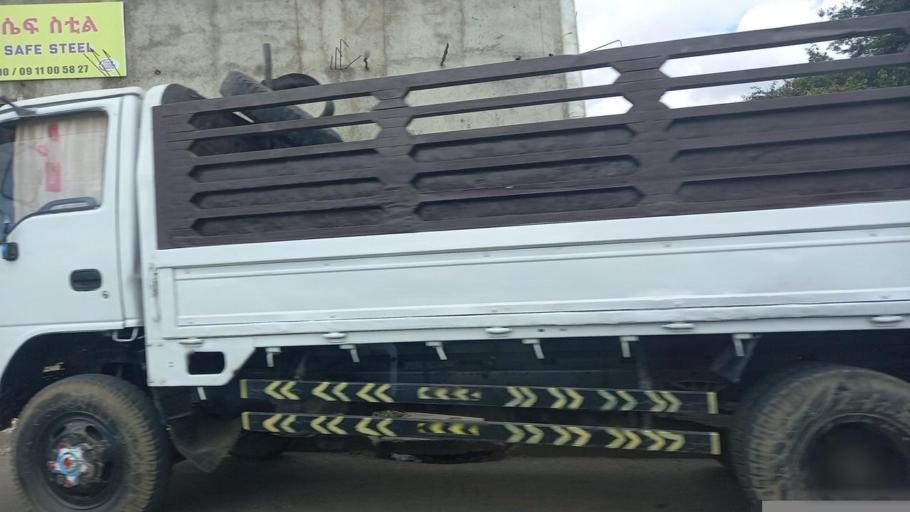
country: ET
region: Adis Abeba
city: Addis Ababa
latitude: 9.0131
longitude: 38.8328
